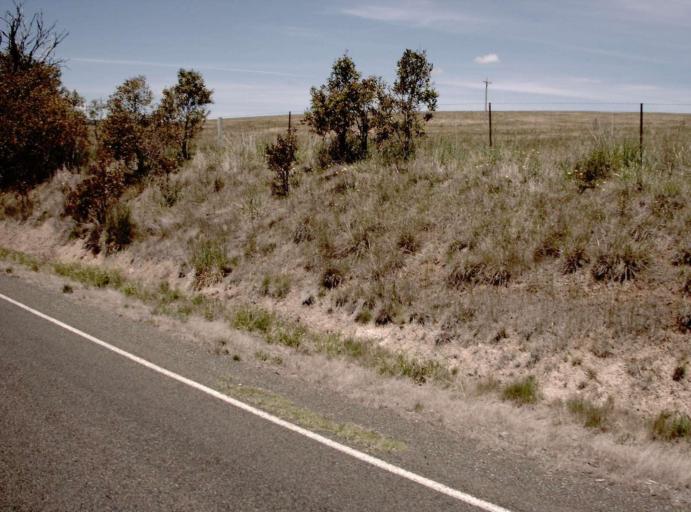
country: AU
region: Victoria
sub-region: Alpine
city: Mount Beauty
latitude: -37.1383
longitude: 147.6460
